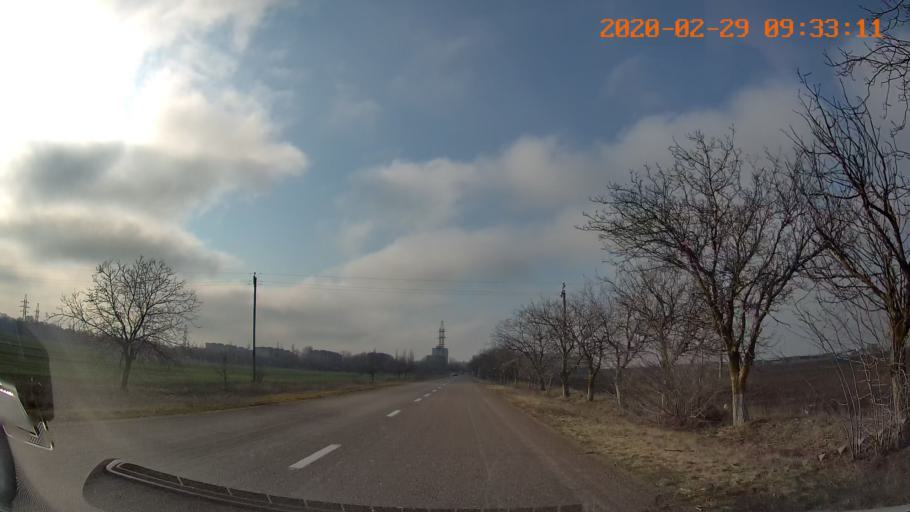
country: MD
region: Telenesti
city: Dnestrovsc
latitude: 46.6305
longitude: 29.9025
